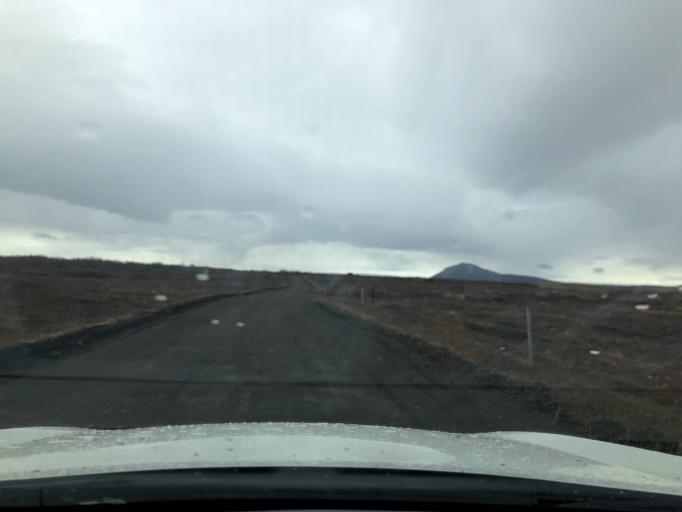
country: IS
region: Northeast
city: Laugar
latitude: 65.6097
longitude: -16.9062
